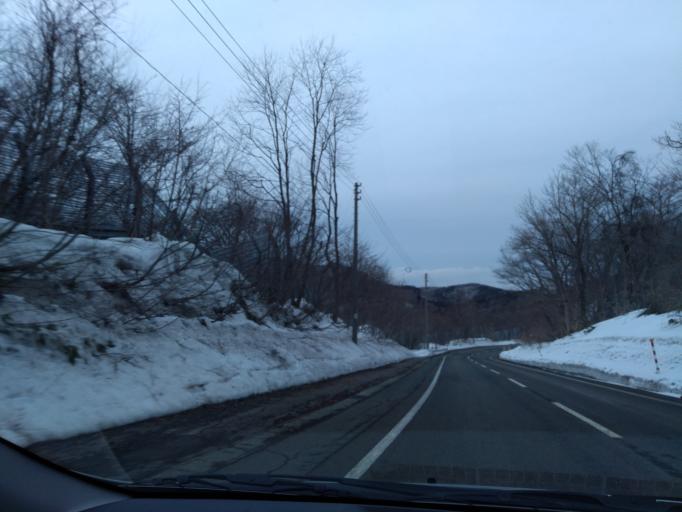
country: JP
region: Iwate
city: Kitakami
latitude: 39.2349
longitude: 140.9453
